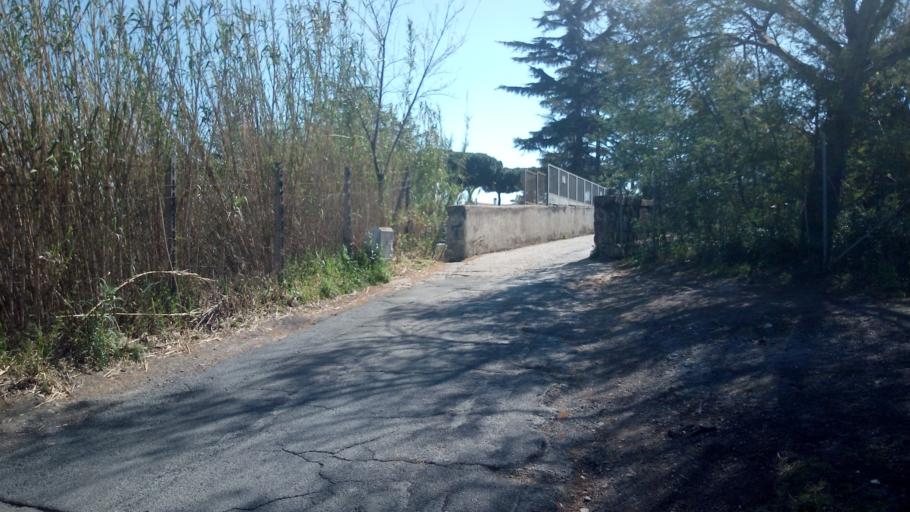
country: IT
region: Latium
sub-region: Citta metropolitana di Roma Capitale
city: Ciampino
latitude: 41.8032
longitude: 12.6049
